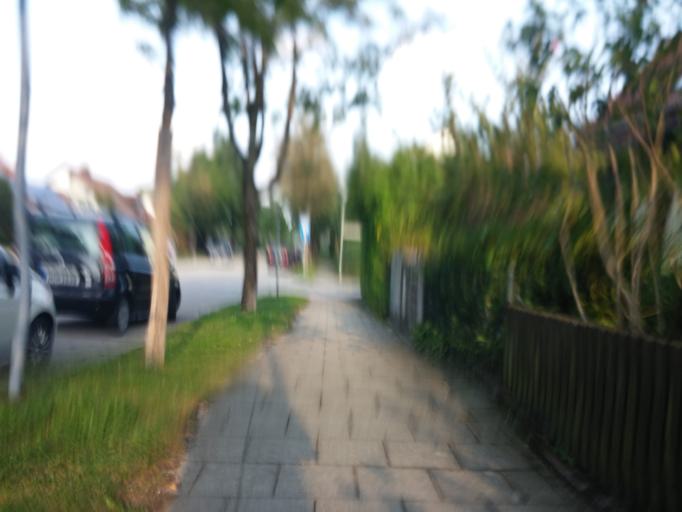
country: DE
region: Bavaria
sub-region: Upper Bavaria
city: Kirchheim bei Muenchen
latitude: 48.1636
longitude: 11.7646
